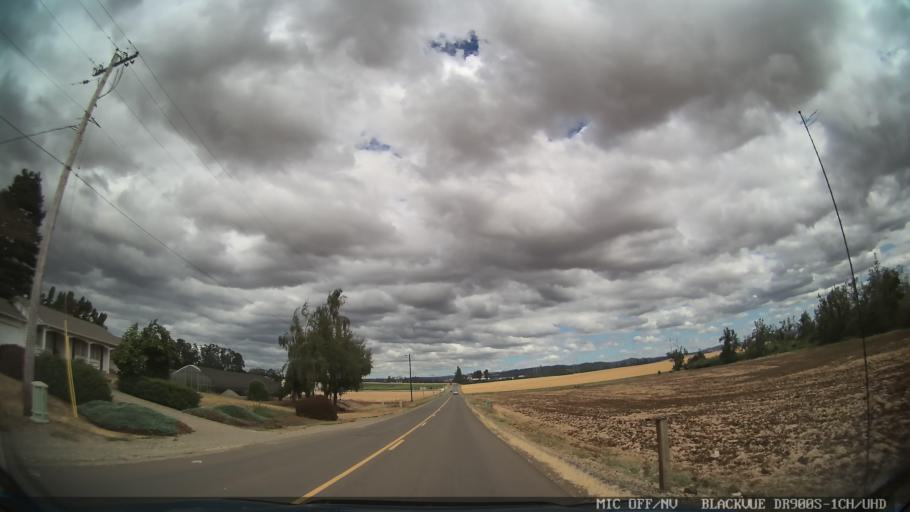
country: US
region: Oregon
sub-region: Marion County
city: Sublimity
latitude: 44.8660
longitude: -122.7863
